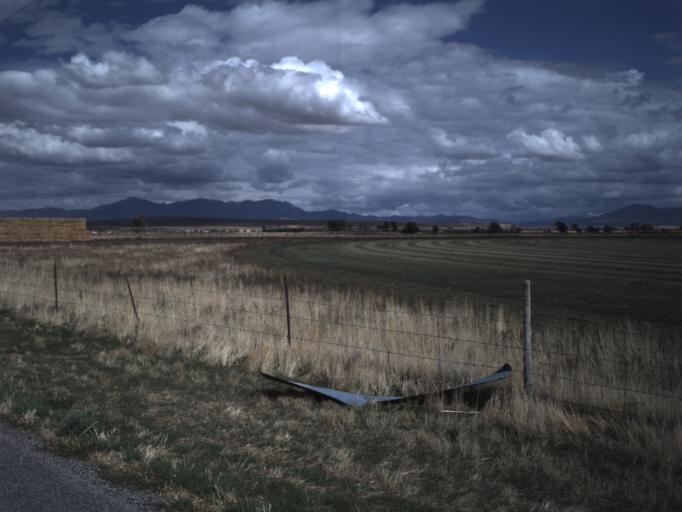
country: US
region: Utah
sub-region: Millard County
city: Fillmore
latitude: 39.0425
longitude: -112.4098
